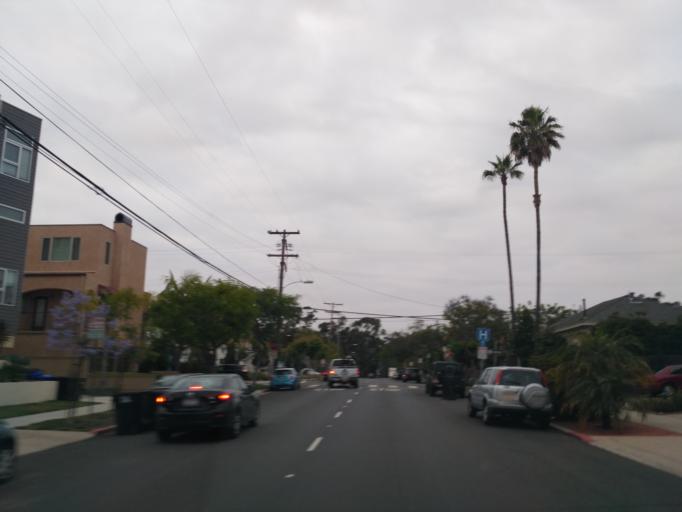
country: US
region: California
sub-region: San Diego County
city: San Diego
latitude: 32.7523
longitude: -117.1641
